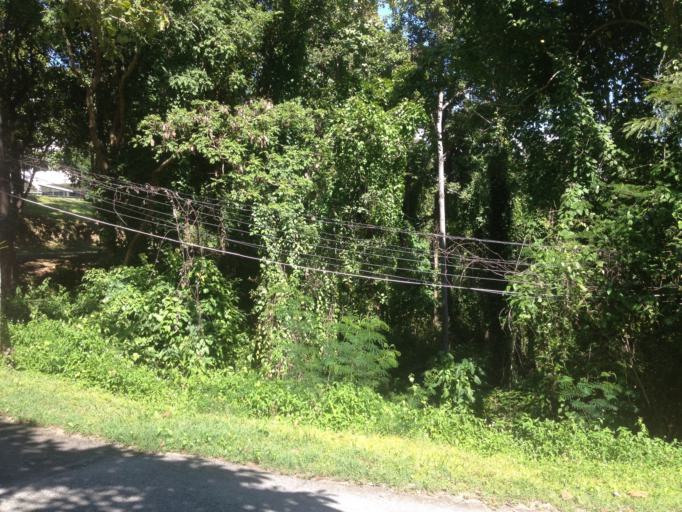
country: TH
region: Chiang Mai
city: Chiang Mai
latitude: 18.7976
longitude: 98.9423
